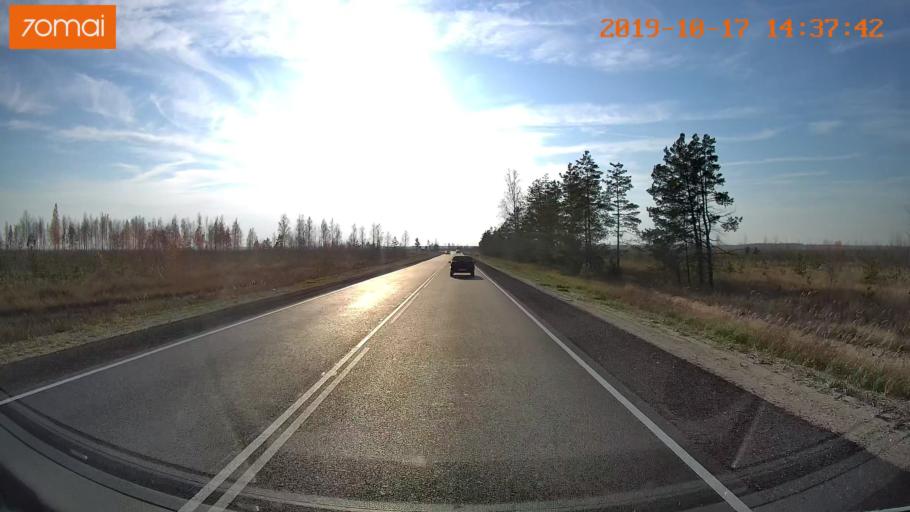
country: RU
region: Rjazan
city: Solotcha
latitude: 54.8776
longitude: 39.9932
